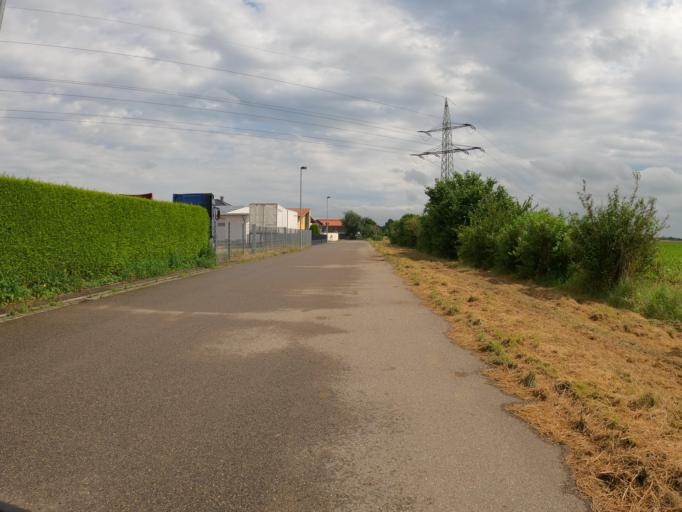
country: DE
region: Baden-Wuerttemberg
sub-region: Tuebingen Region
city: Langenau
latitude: 48.4867
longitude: 10.1248
